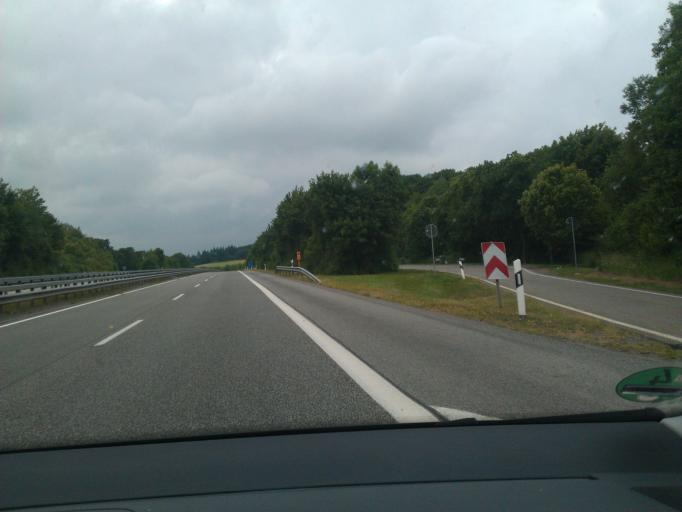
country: DE
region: Rheinland-Pfalz
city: Rohrbach
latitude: 49.5689
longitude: 7.2541
